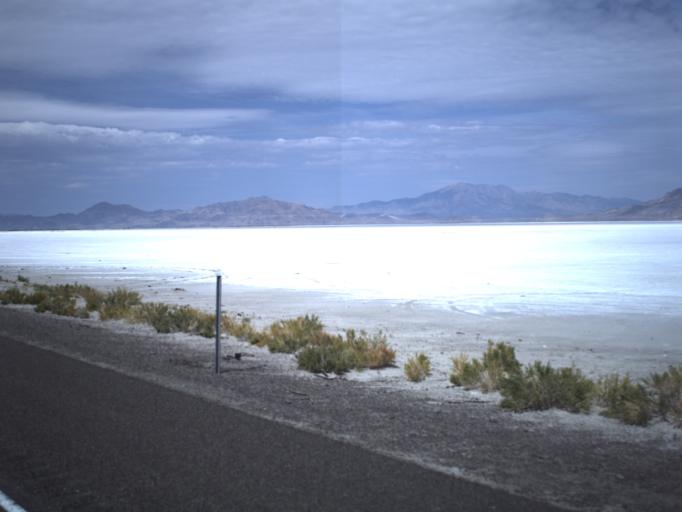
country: US
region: Utah
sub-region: Tooele County
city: Wendover
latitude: 40.7367
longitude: -113.7182
